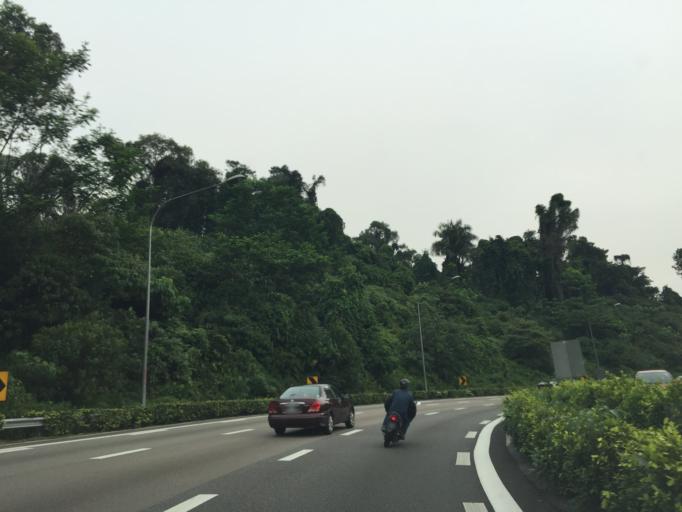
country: SG
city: Singapore
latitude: 1.3479
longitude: 103.7934
